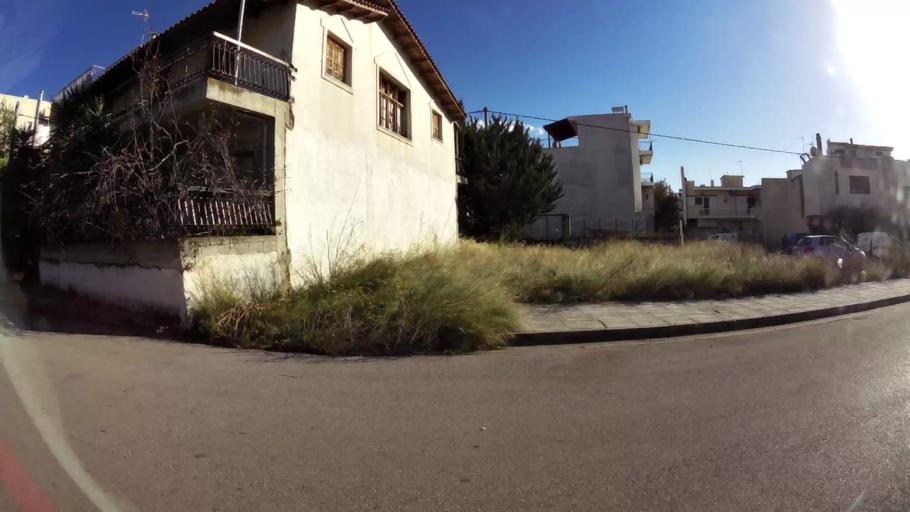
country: GR
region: Attica
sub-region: Nomarchia Anatolikis Attikis
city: Acharnes
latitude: 38.0926
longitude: 23.7353
